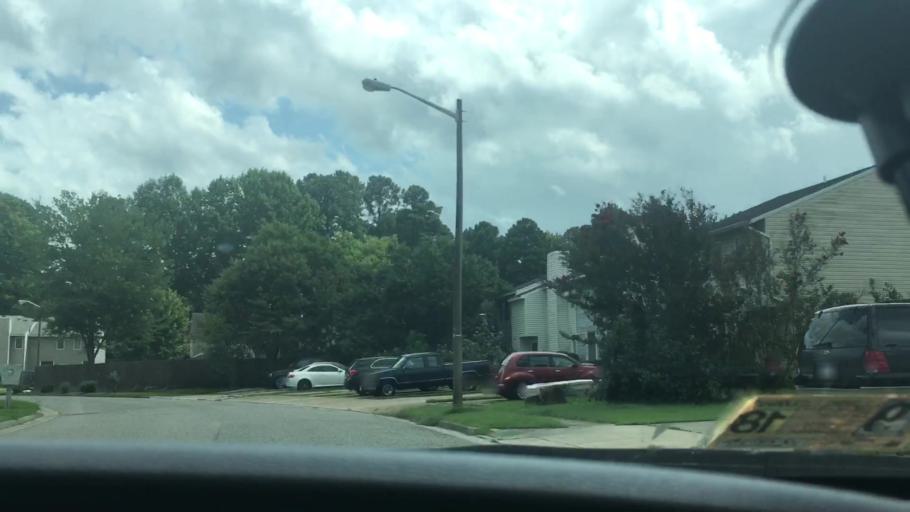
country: US
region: Virginia
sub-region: City of Portsmouth
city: Portsmouth Heights
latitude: 36.8586
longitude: -76.4104
